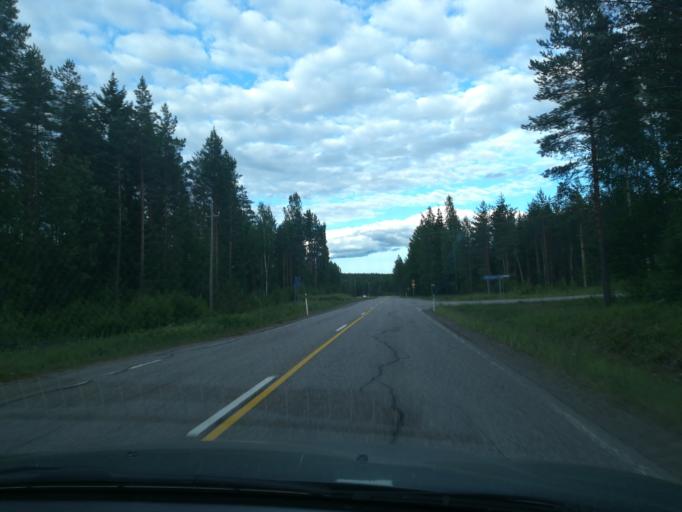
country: FI
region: Southern Savonia
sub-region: Mikkeli
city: Puumala
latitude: 61.5601
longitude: 28.0268
